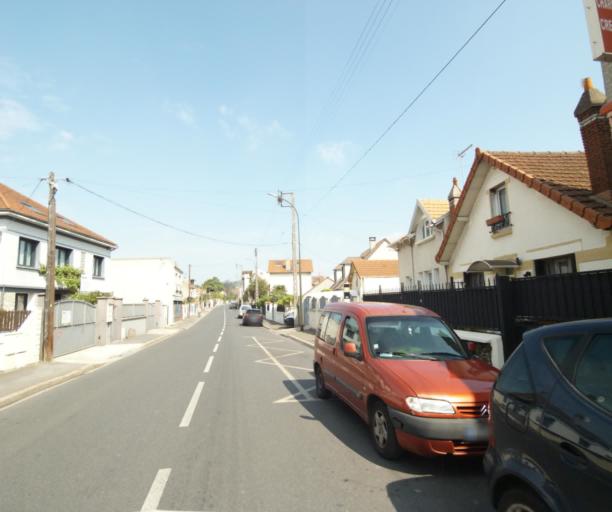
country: FR
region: Ile-de-France
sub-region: Departement du Val-d'Oise
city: Argenteuil
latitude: 48.9552
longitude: 2.2420
